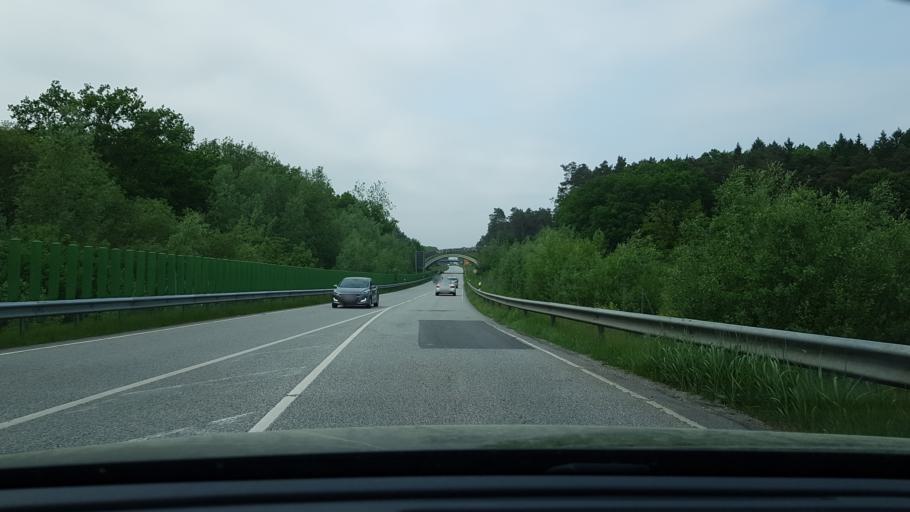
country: DE
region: Schleswig-Holstein
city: Gross Sarau
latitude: 53.7863
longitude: 10.7043
